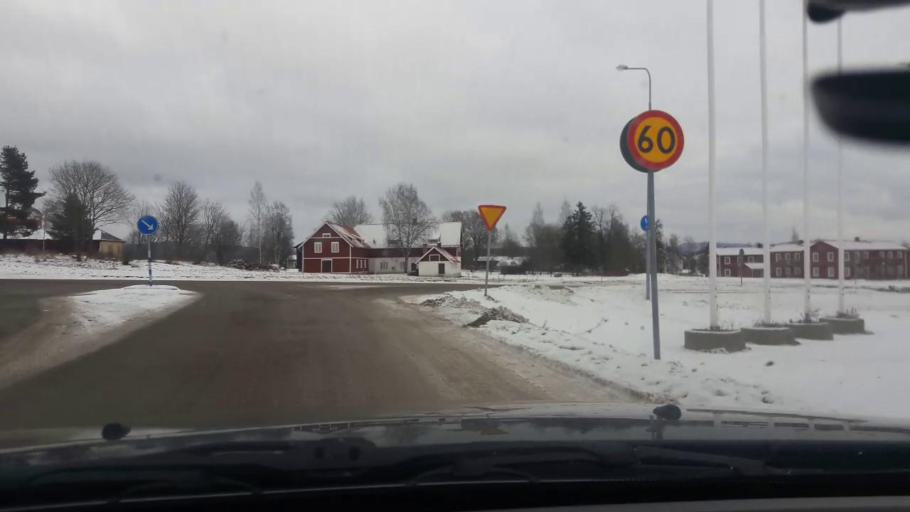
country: SE
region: Gaevleborg
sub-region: Bollnas Kommun
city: Bollnas
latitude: 61.3439
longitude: 16.3837
